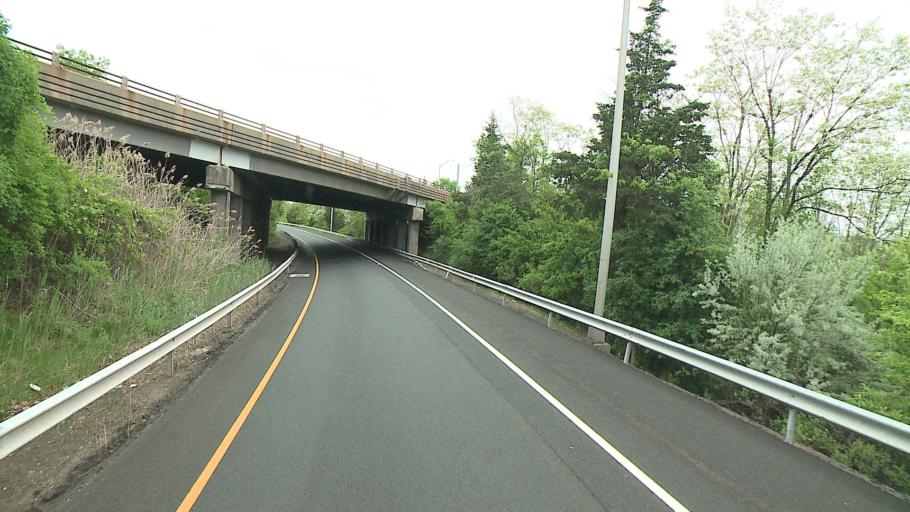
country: US
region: Connecticut
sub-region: Hartford County
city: Farmington
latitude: 41.7207
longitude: -72.7944
